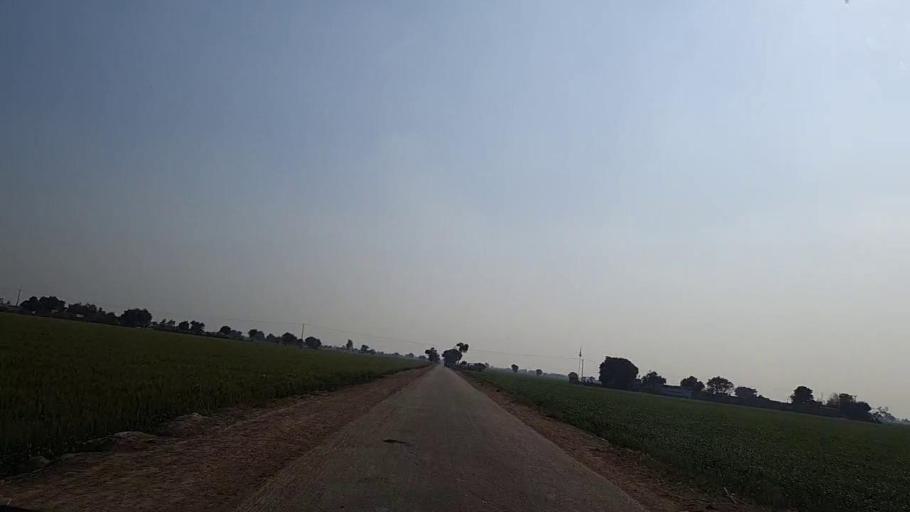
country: PK
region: Sindh
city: Sakrand
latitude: 26.0957
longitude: 68.2904
